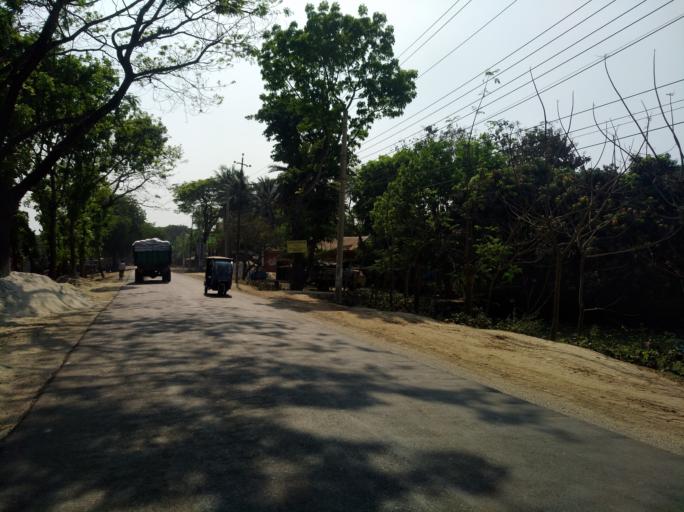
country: BD
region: Khulna
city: Kaliganj
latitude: 23.5524
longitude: 89.1723
